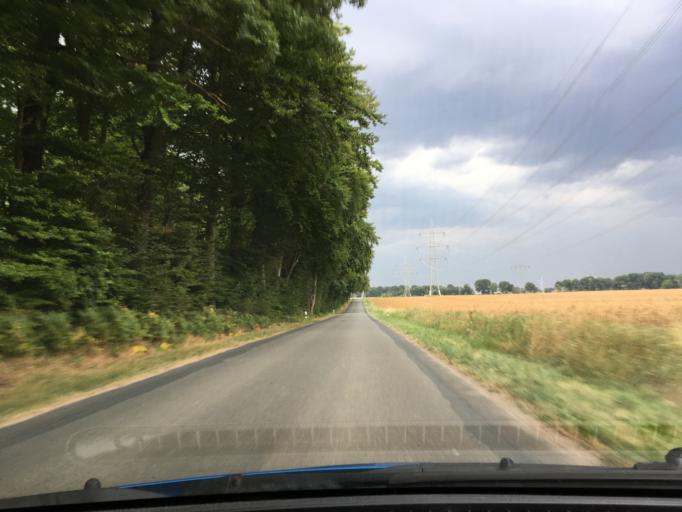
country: DE
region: Lower Saxony
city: Hanstedt Eins
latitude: 53.0796
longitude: 10.3861
